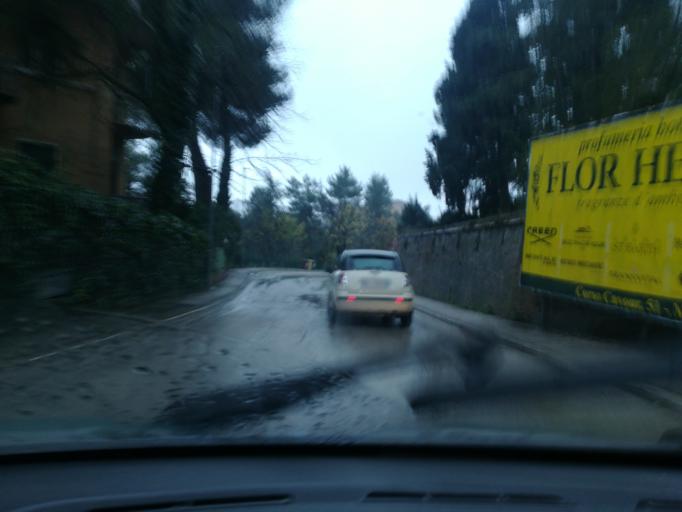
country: IT
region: The Marches
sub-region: Provincia di Macerata
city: Macerata
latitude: 43.2980
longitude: 13.4367
